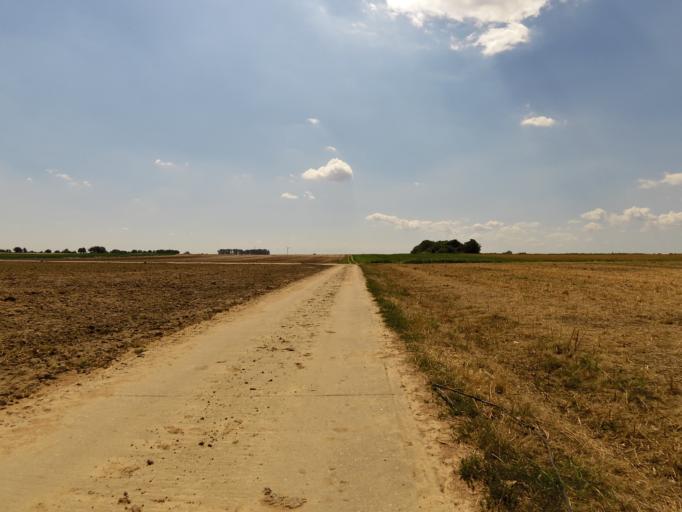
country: DE
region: Rheinland-Pfalz
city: Fussgonheim
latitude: 49.4497
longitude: 8.2824
